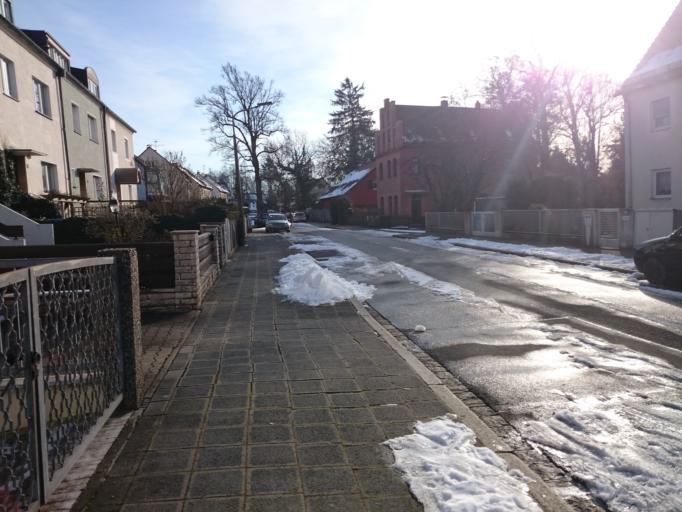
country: DE
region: Bavaria
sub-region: Regierungsbezirk Mittelfranken
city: Nuernberg
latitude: 49.4418
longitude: 11.1276
